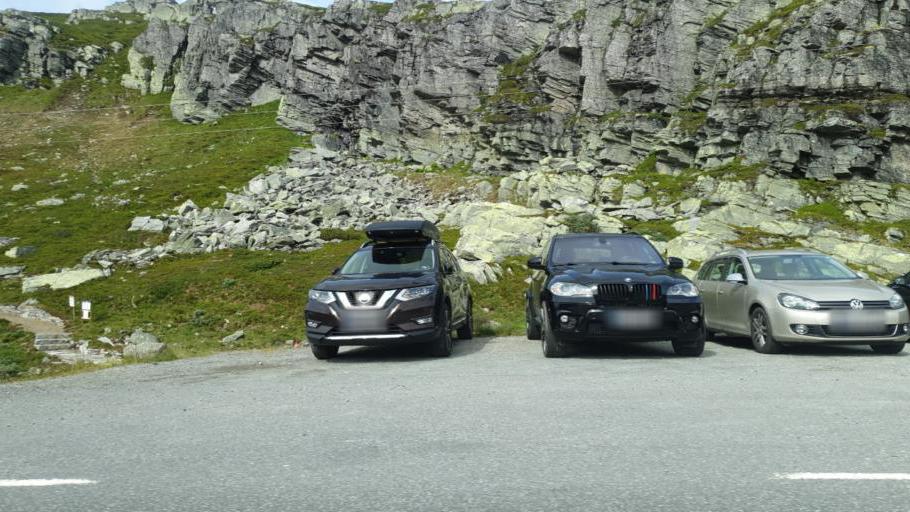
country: NO
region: Oppland
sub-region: Vestre Slidre
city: Slidre
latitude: 61.2899
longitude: 8.8132
